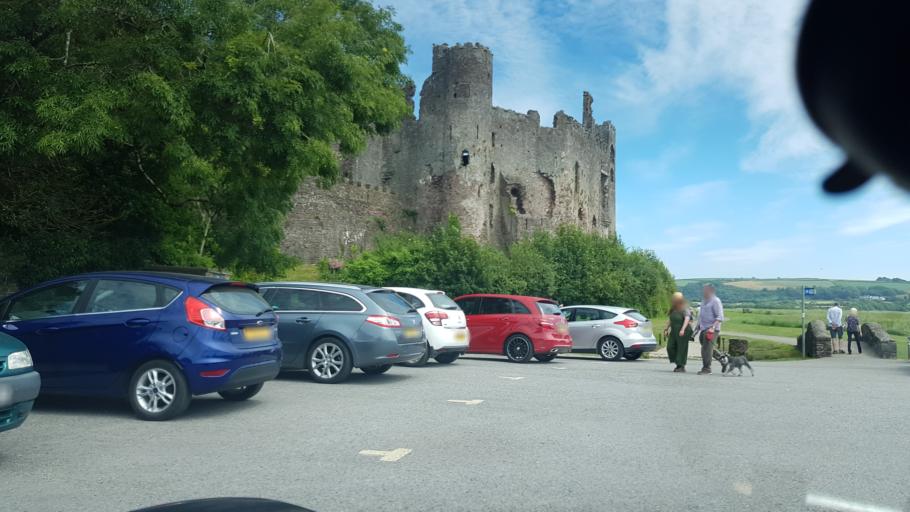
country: GB
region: Wales
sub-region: Carmarthenshire
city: Saint Clears
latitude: 51.7690
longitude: -4.4632
